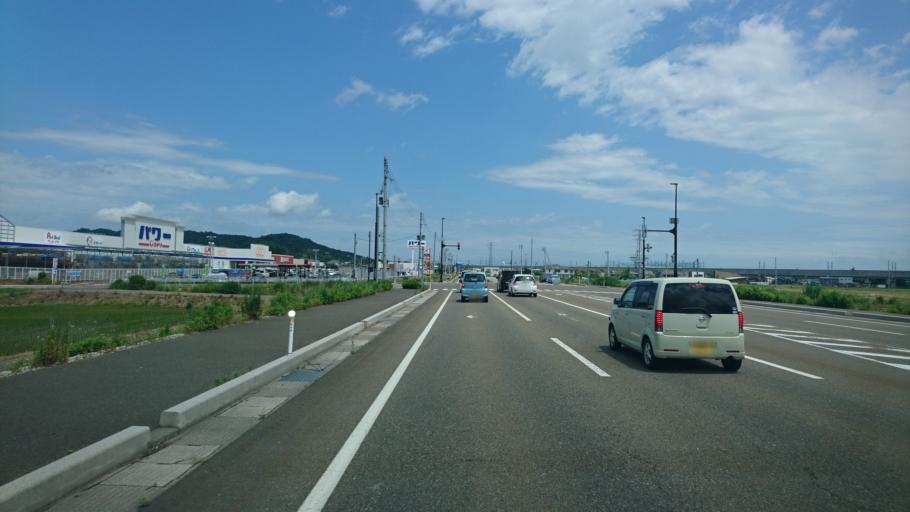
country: JP
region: Niigata
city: Joetsu
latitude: 37.0879
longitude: 138.2335
